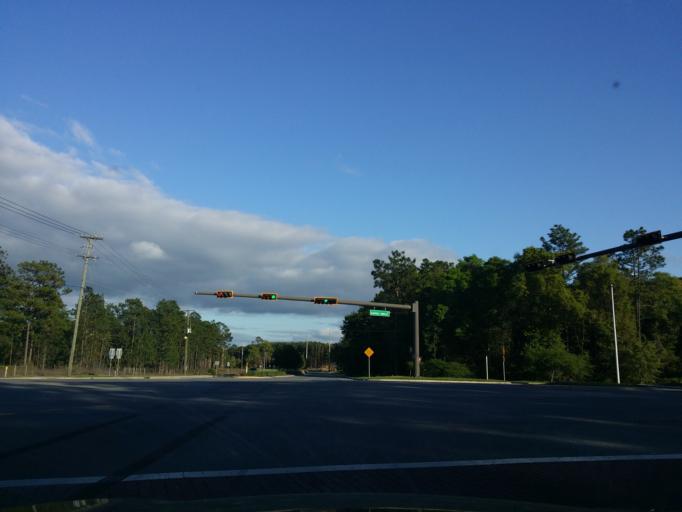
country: US
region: Florida
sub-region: Leon County
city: Woodville
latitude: 30.3813
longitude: -84.2370
